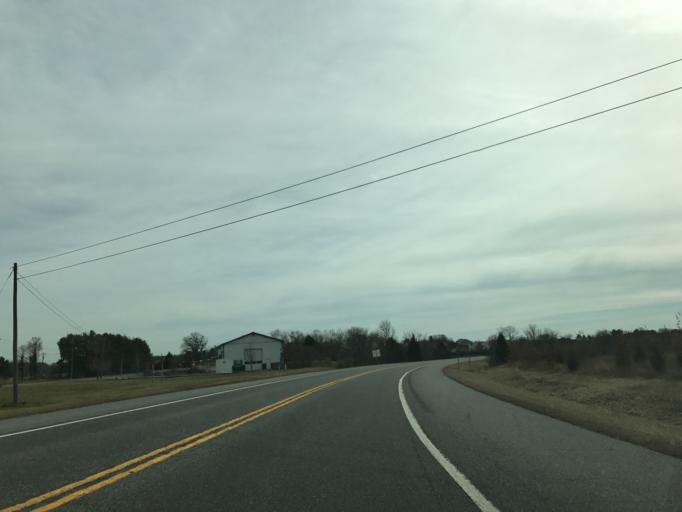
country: US
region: Maryland
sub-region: Queen Anne's County
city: Kingstown
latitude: 39.1536
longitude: -75.9811
